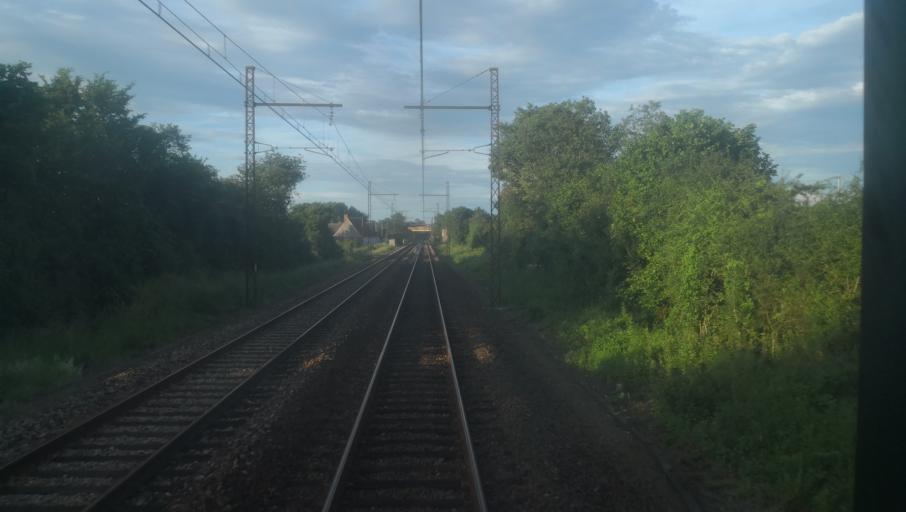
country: FR
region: Centre
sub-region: Departement de l'Indre
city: Le Pechereau
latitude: 46.5202
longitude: 1.5086
